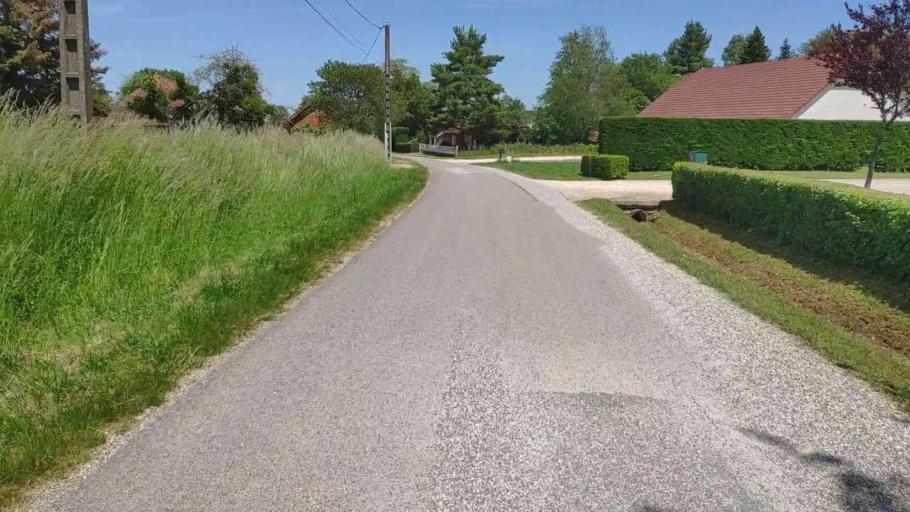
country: FR
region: Franche-Comte
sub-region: Departement du Jura
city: Bletterans
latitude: 46.7922
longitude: 5.3765
